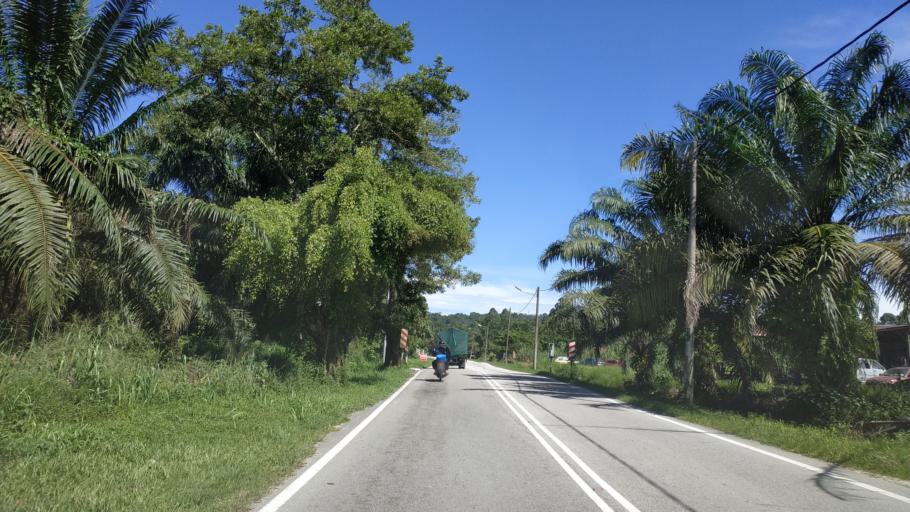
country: MY
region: Kedah
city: Kulim
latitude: 5.3142
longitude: 100.5402
